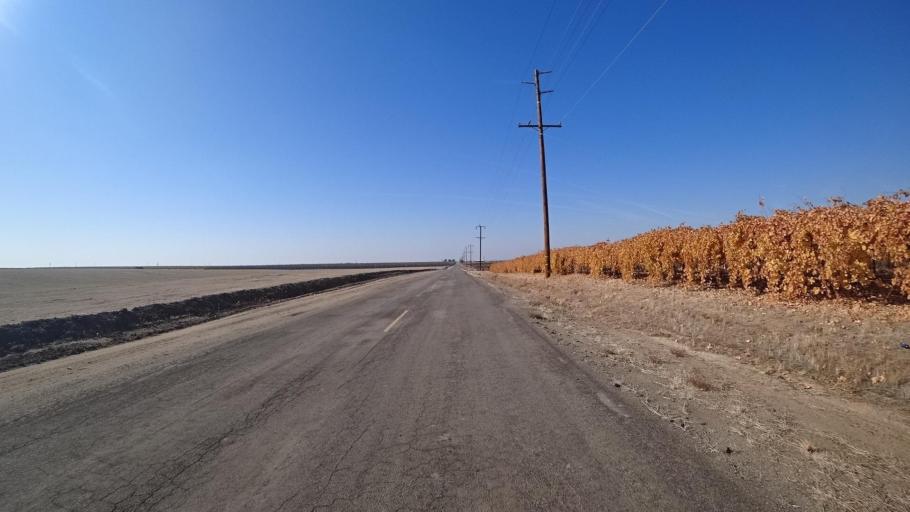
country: US
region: California
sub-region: Kern County
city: McFarland
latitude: 35.7035
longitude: -119.1371
